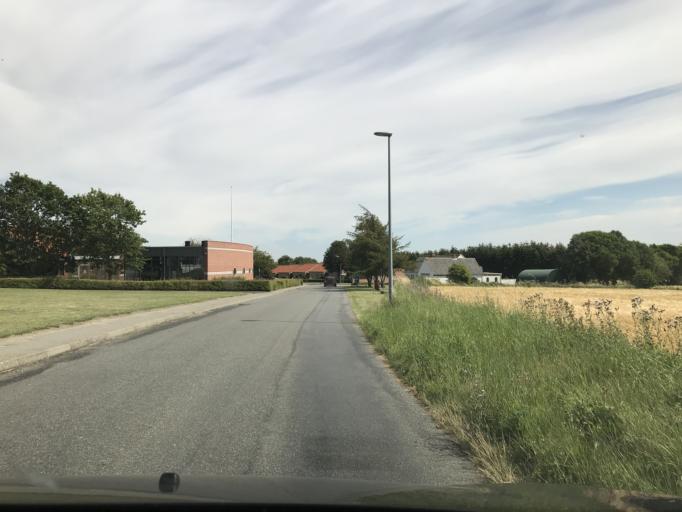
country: DK
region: South Denmark
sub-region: AEro Kommune
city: Marstal
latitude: 54.8505
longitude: 10.5092
